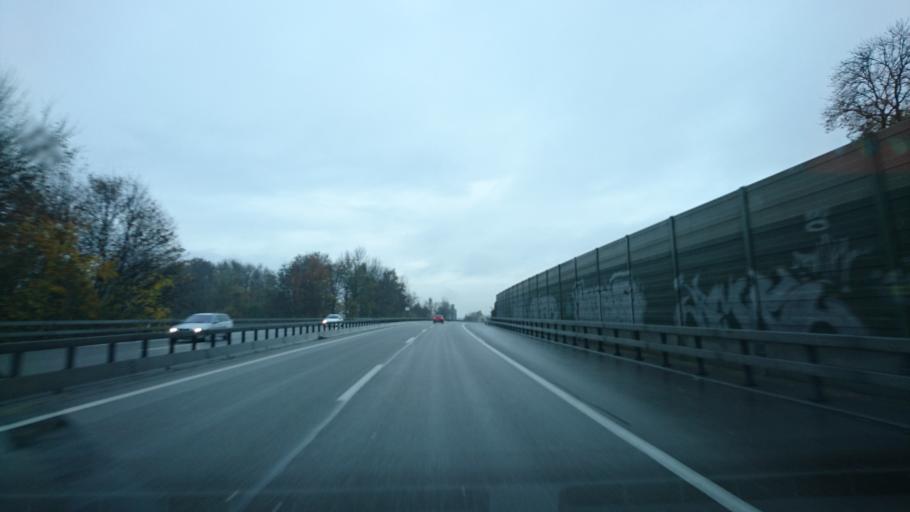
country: CH
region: Bern
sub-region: Emmental District
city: Kirchberg
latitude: 47.0901
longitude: 7.5732
